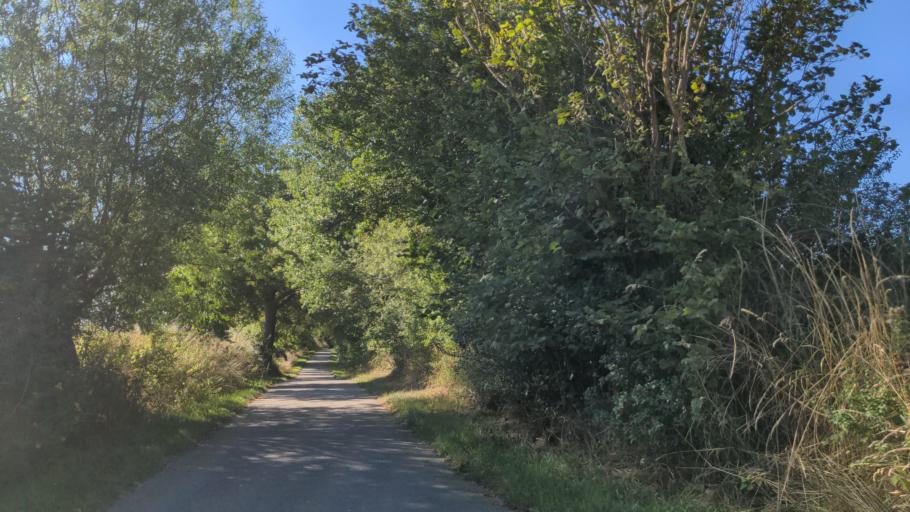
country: DE
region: Mecklenburg-Vorpommern
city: Ostseebad Boltenhagen
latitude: 54.0065
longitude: 11.1867
